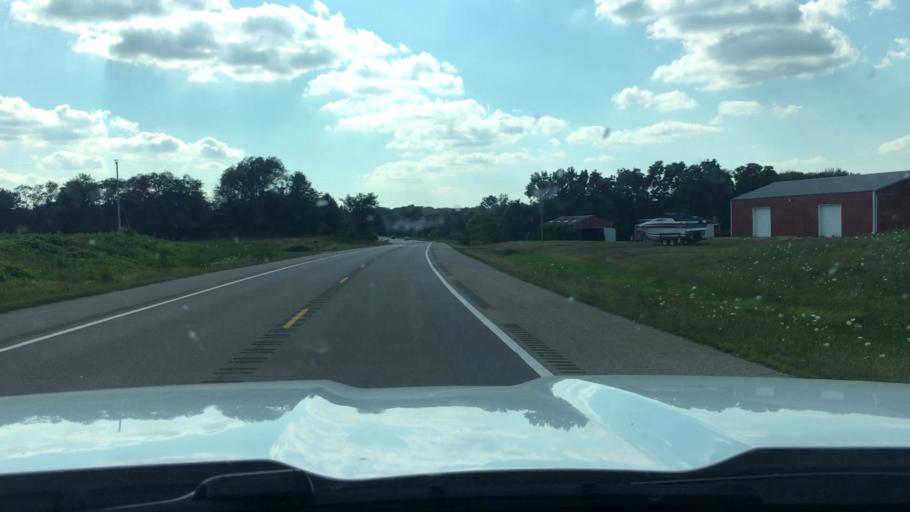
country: US
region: Michigan
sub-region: Ionia County
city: Belding
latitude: 43.0822
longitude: -85.3795
